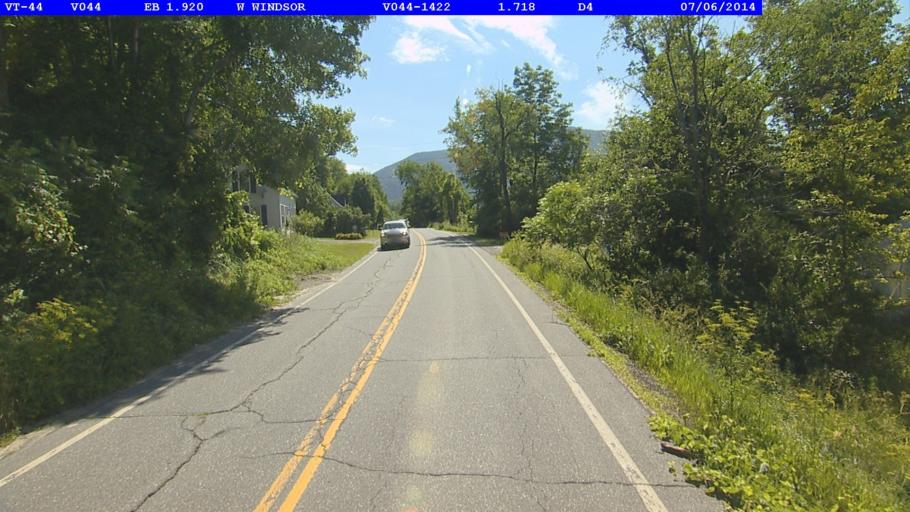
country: US
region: Vermont
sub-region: Windsor County
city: Windsor
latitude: 43.4536
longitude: -72.5088
